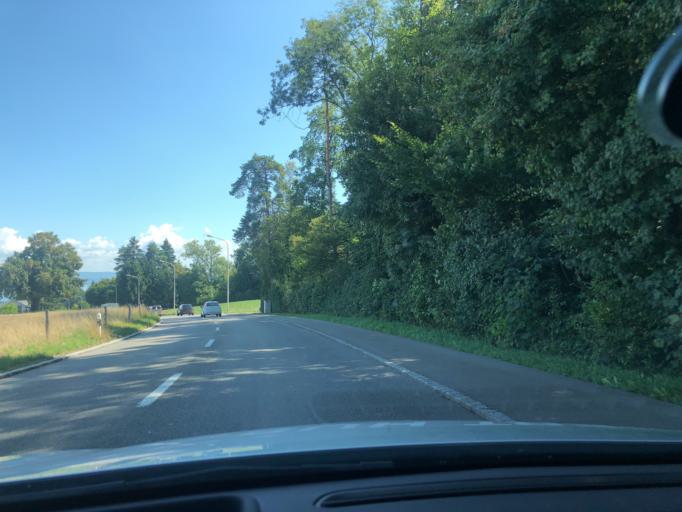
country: CH
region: Thurgau
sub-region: Kreuzlingen District
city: Kreuzlingen
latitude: 47.6373
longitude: 9.1589
